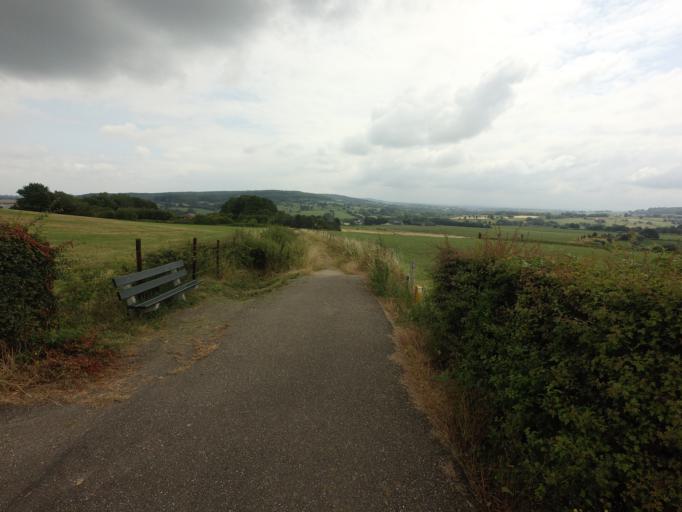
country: BE
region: Wallonia
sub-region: Province de Liege
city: Plombieres
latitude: 50.7744
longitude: 5.9038
